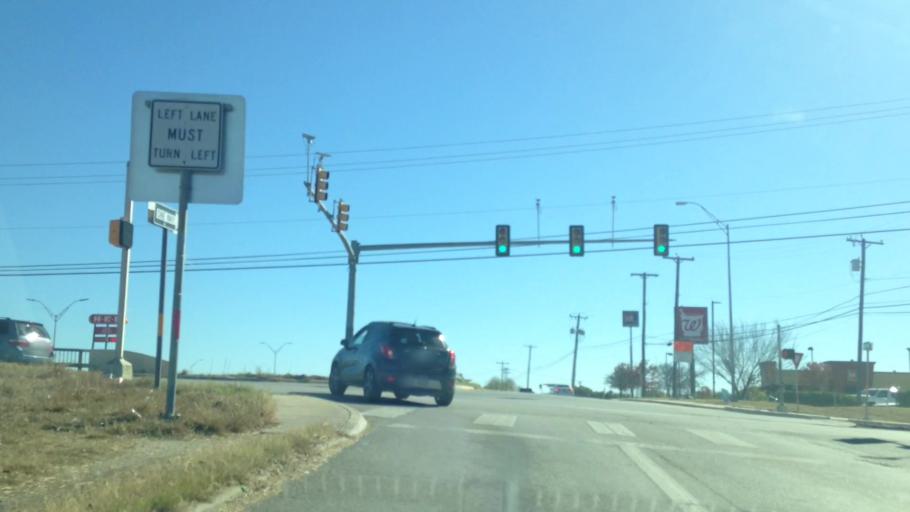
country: US
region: Texas
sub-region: Bexar County
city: Lackland Air Force Base
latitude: 29.3805
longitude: -98.6421
